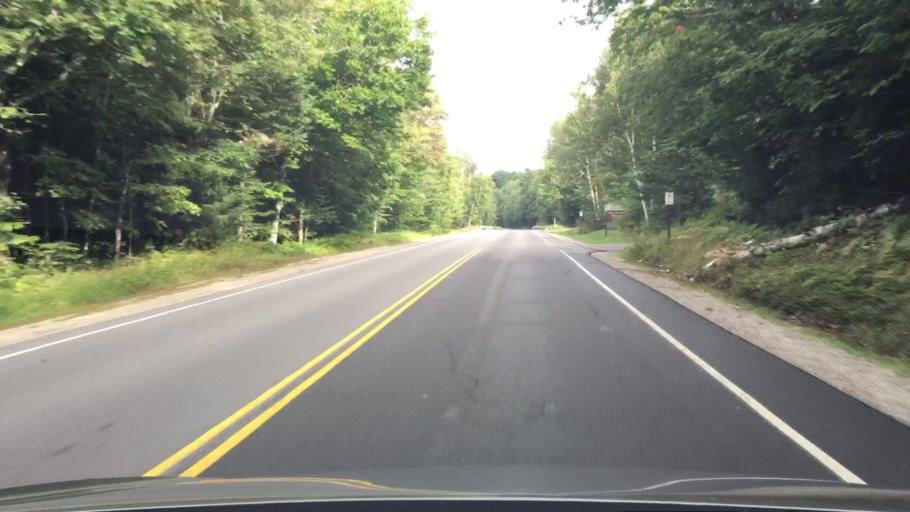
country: US
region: New Hampshire
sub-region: Carroll County
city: Tamworth
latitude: 43.9978
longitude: -71.3940
